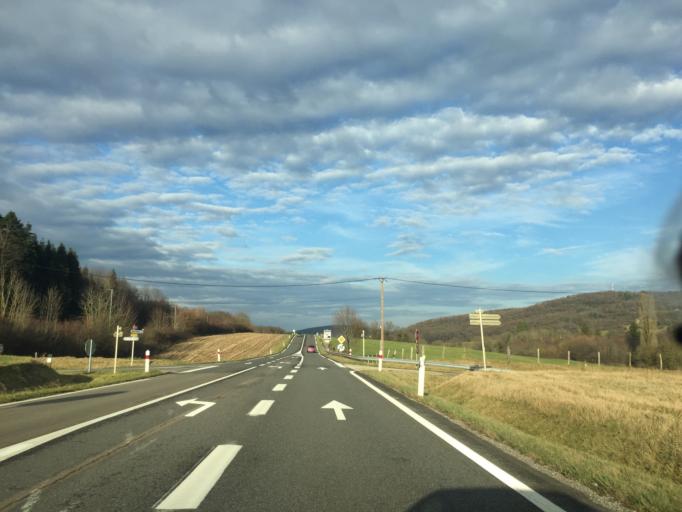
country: FR
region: Franche-Comte
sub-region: Departement du Jura
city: Mouchard
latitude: 46.9454
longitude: 5.7809
